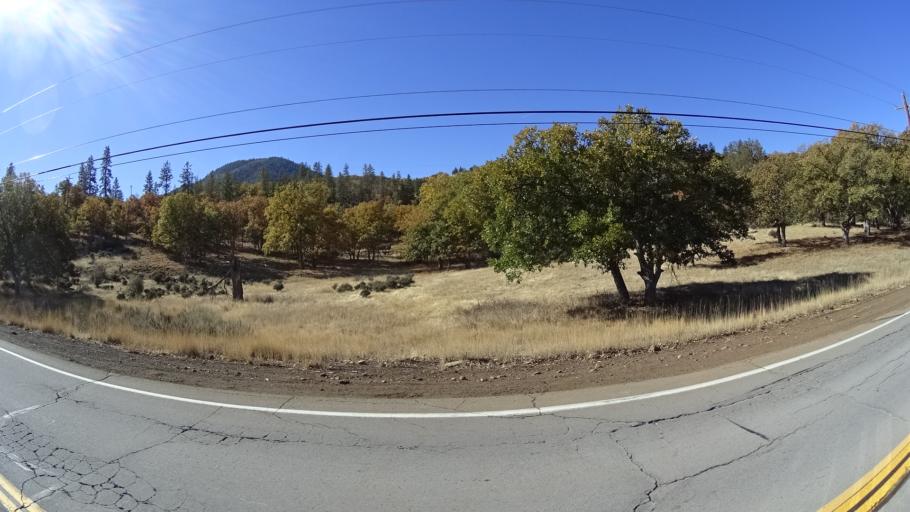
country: US
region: California
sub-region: Siskiyou County
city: Montague
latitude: 41.8914
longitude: -122.4997
